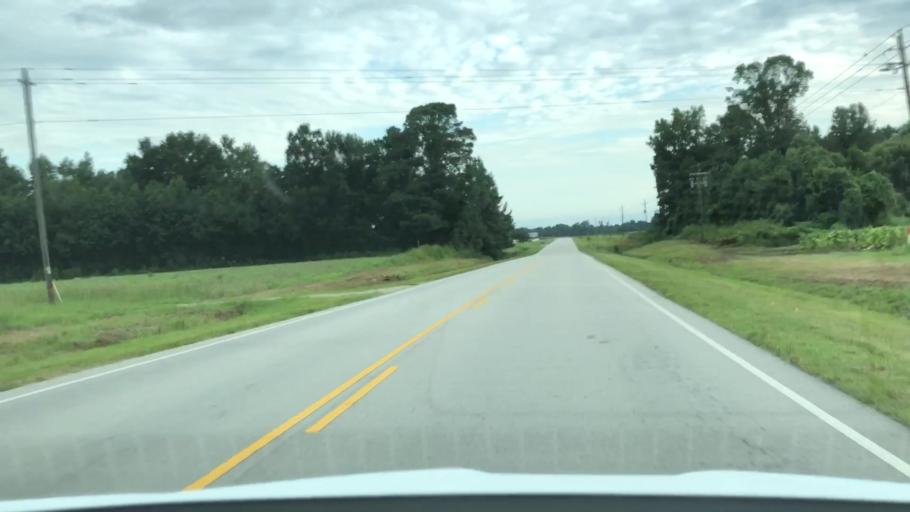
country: US
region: North Carolina
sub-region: Jones County
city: Trenton
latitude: 35.0416
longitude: -77.3502
